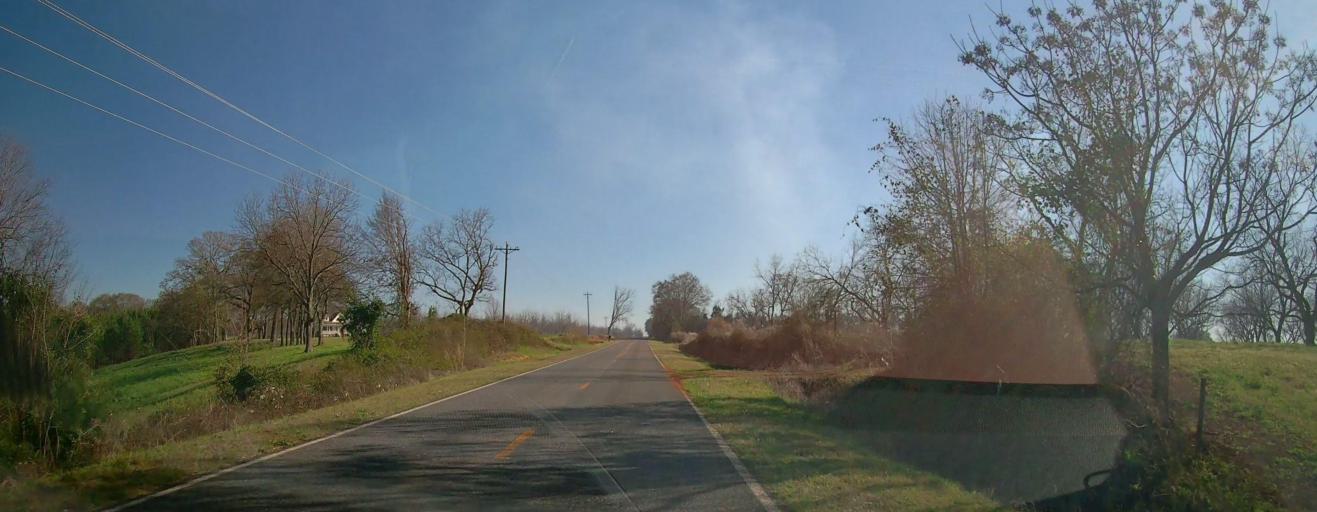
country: US
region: Georgia
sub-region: Peach County
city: Fort Valley
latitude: 32.6132
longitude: -83.8522
